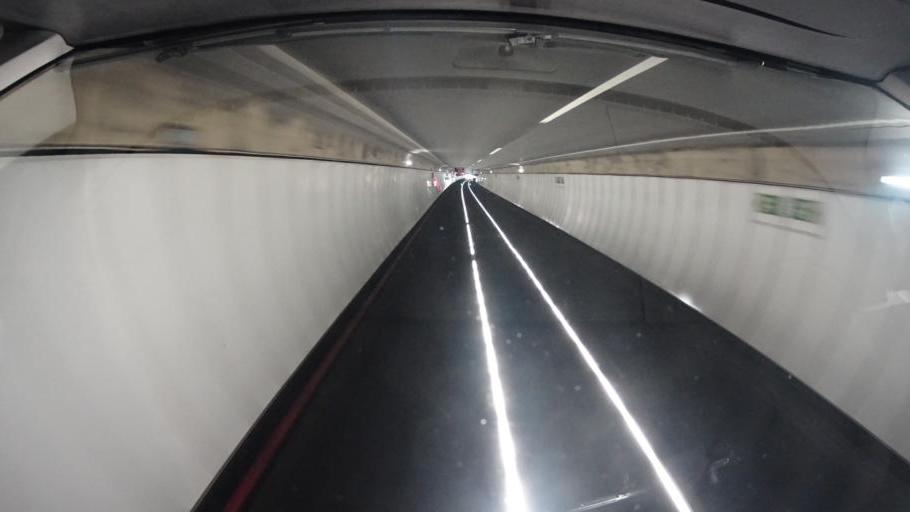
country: ES
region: Basque Country
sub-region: Bizkaia
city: Basauri
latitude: 43.2324
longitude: -2.8976
